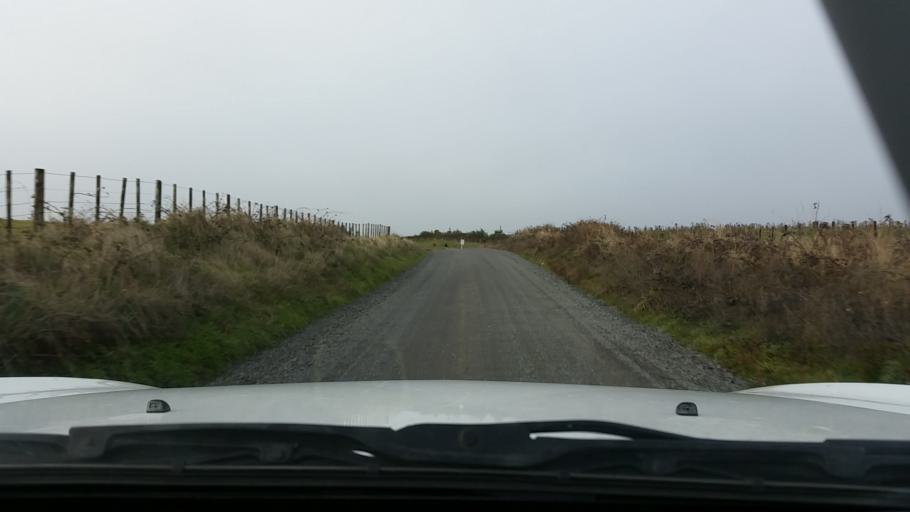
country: NZ
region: Bay of Plenty
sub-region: Rotorua District
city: Rotorua
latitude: -38.1565
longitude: 176.0850
